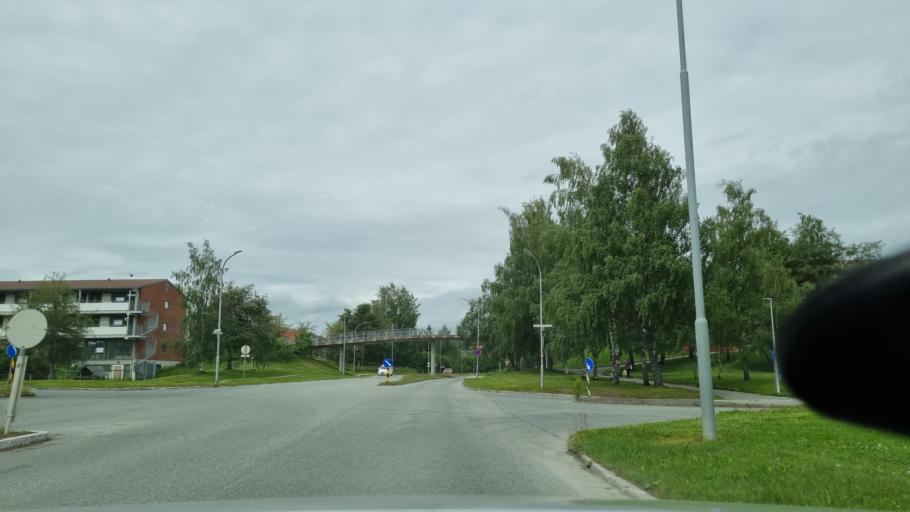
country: NO
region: Sor-Trondelag
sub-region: Melhus
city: Melhus
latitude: 63.3466
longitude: 10.3344
